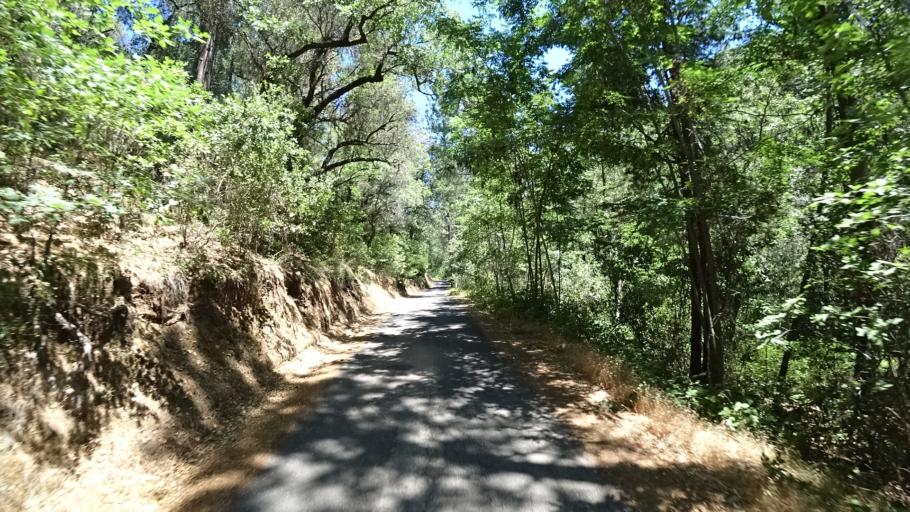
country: US
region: California
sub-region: Calaveras County
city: Forest Meadows
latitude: 38.1393
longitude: -120.4212
